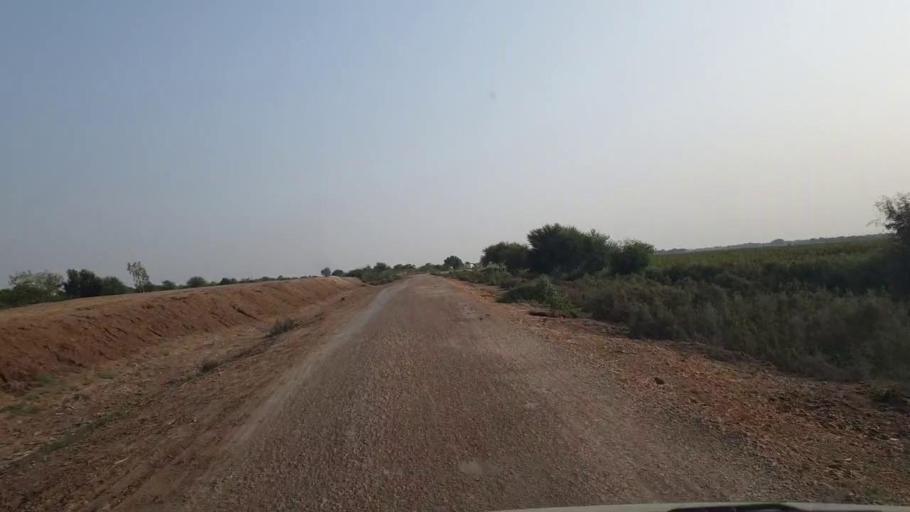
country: PK
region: Sindh
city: Matli
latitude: 25.0516
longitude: 68.7644
